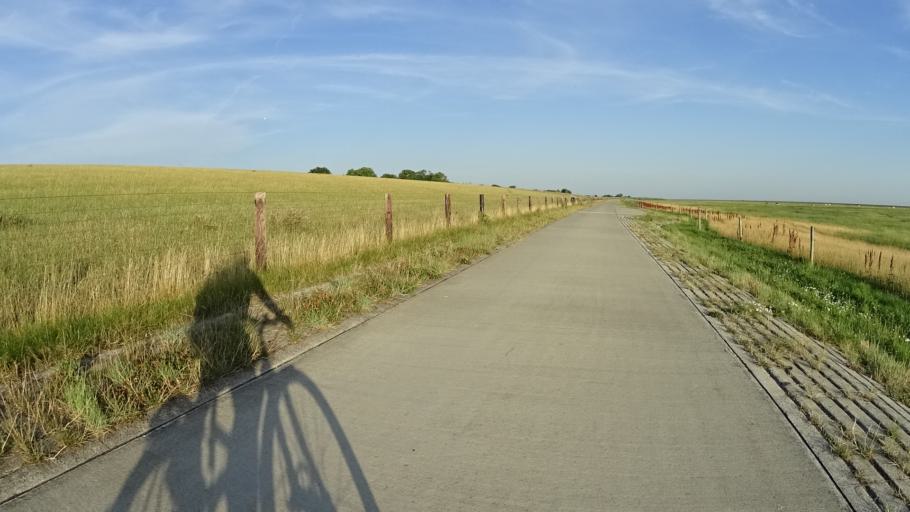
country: DE
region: Lower Saxony
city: Butjadingen
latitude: 53.6043
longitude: 8.3411
